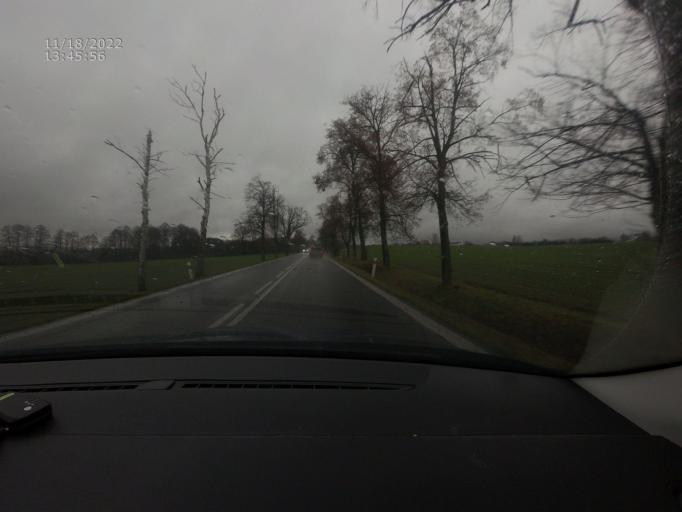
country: CZ
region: Jihocesky
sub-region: Okres Strakonice
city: Blatna
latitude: 49.4267
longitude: 13.8569
